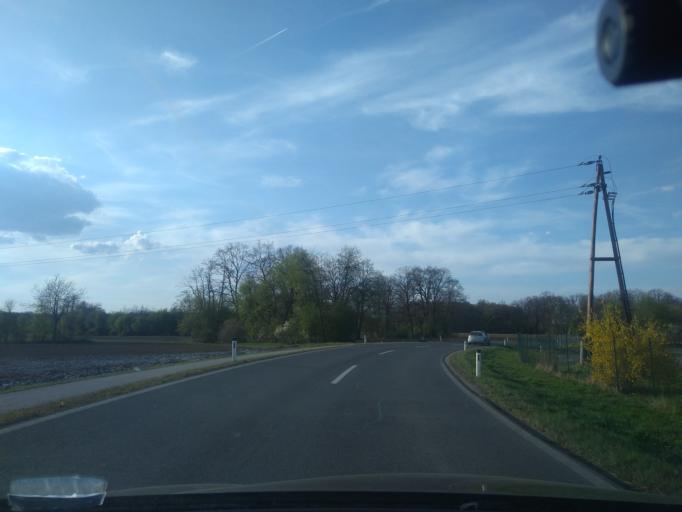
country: AT
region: Styria
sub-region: Politischer Bezirk Suedoststeiermark
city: Mureck
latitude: 46.7142
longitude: 15.7680
